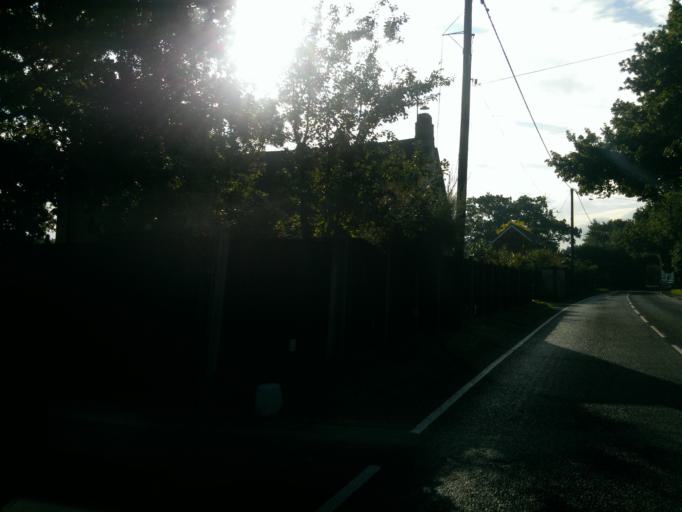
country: GB
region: England
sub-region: Essex
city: Alresford
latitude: 51.8646
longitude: 0.9938
